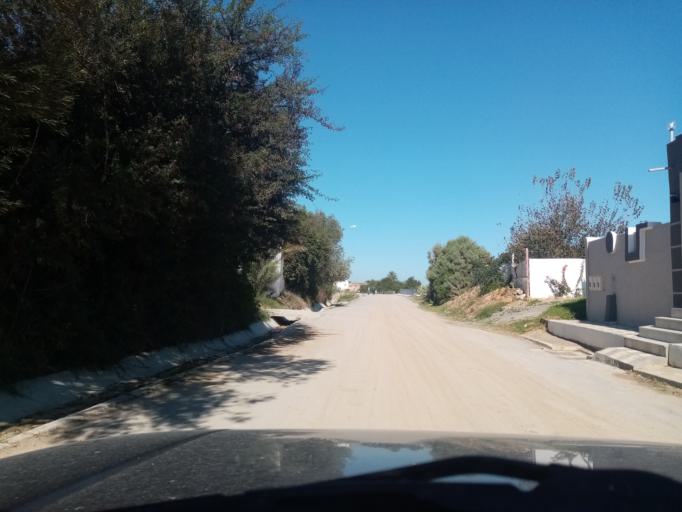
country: TN
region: Nabul
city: Bu `Urqub
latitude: 36.5790
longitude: 10.5707
